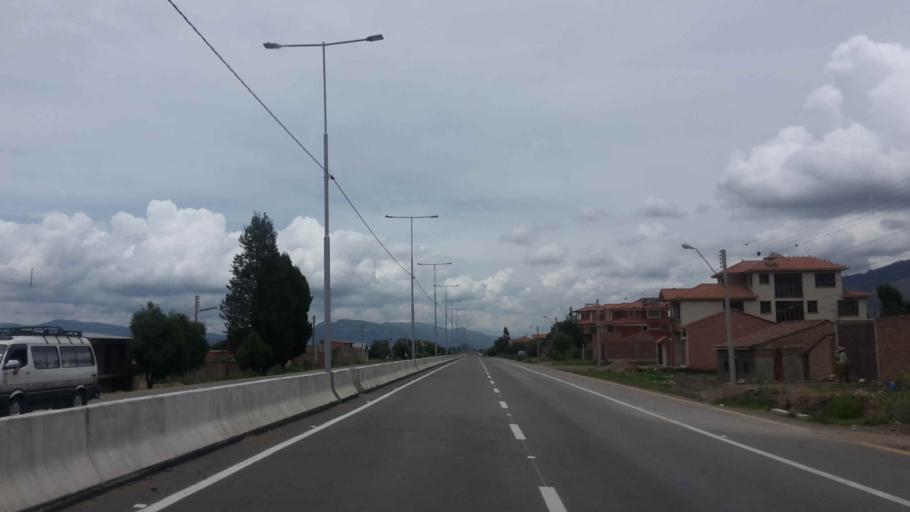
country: BO
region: Cochabamba
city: Cliza
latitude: -17.5265
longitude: -65.9131
